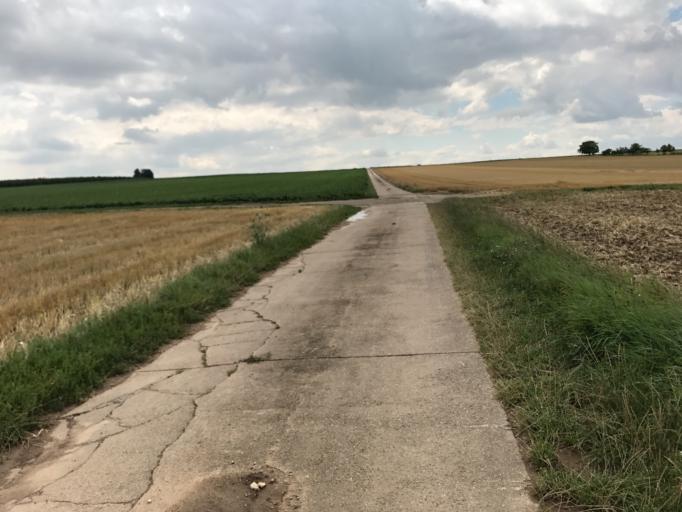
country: DE
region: Rheinland-Pfalz
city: Essenheim
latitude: 49.9451
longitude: 8.1503
